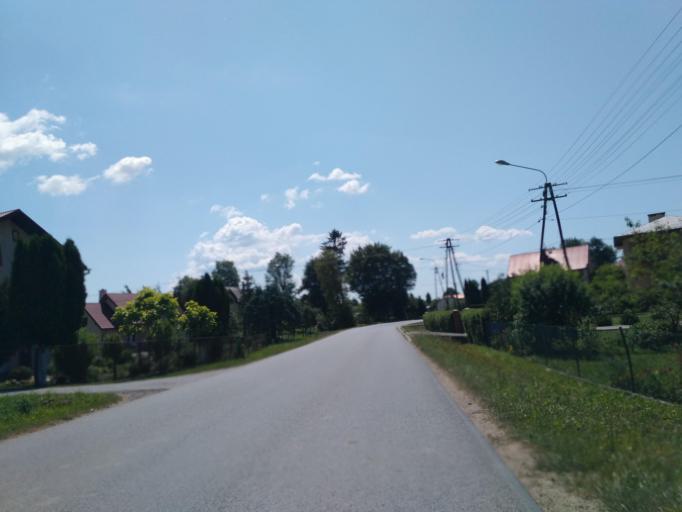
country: PL
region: Subcarpathian Voivodeship
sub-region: Powiat sanocki
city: Niebieszczany
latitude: 49.5316
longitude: 22.1270
